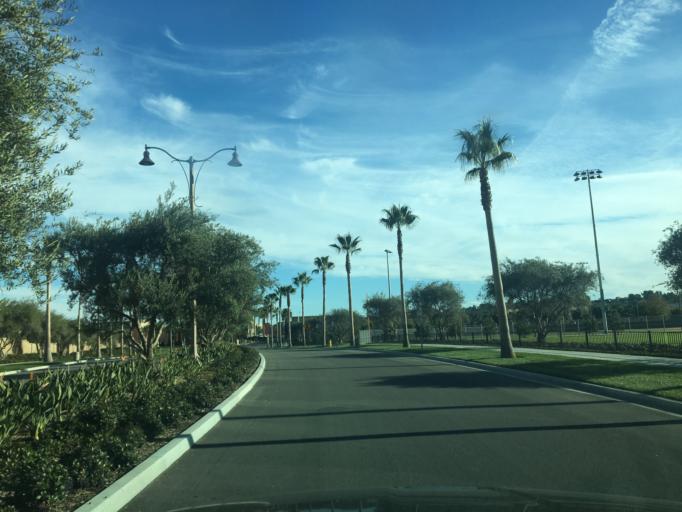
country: US
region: California
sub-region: Orange County
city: Laguna Woods
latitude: 33.6374
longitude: -117.7445
